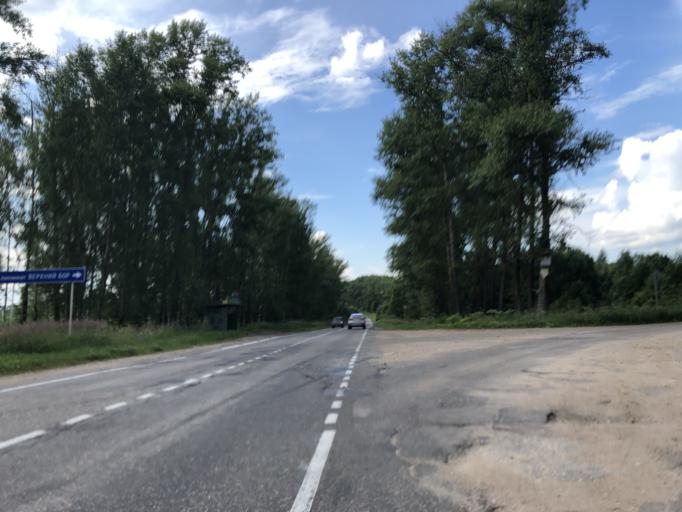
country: RU
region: Tverskaya
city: Rzhev
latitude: 56.2653
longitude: 34.2511
